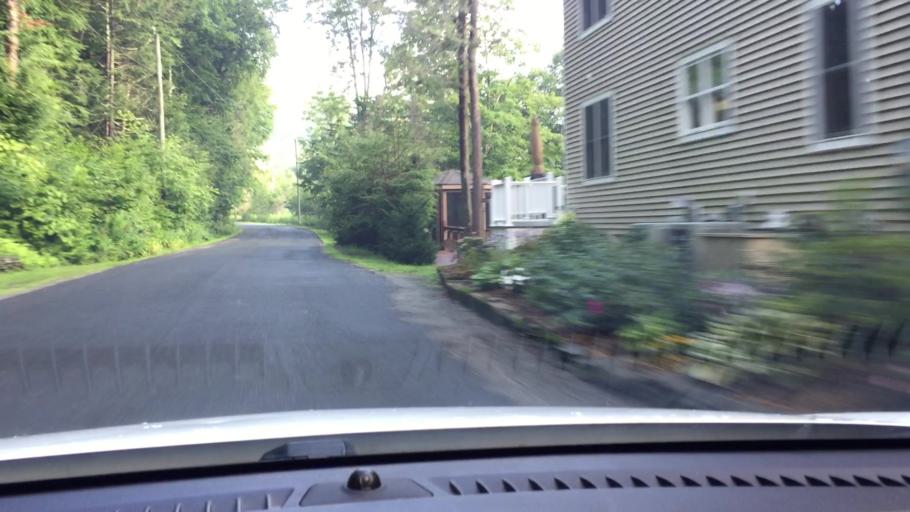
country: US
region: Massachusetts
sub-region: Berkshire County
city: Becket
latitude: 42.3622
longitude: -72.9669
